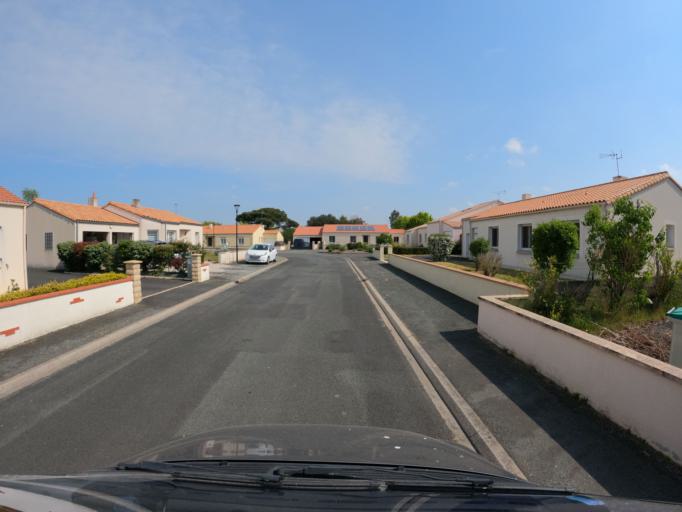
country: FR
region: Pays de la Loire
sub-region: Departement de la Vendee
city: Saint-Hilaire-de-Loulay
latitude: 46.9964
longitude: -1.3325
